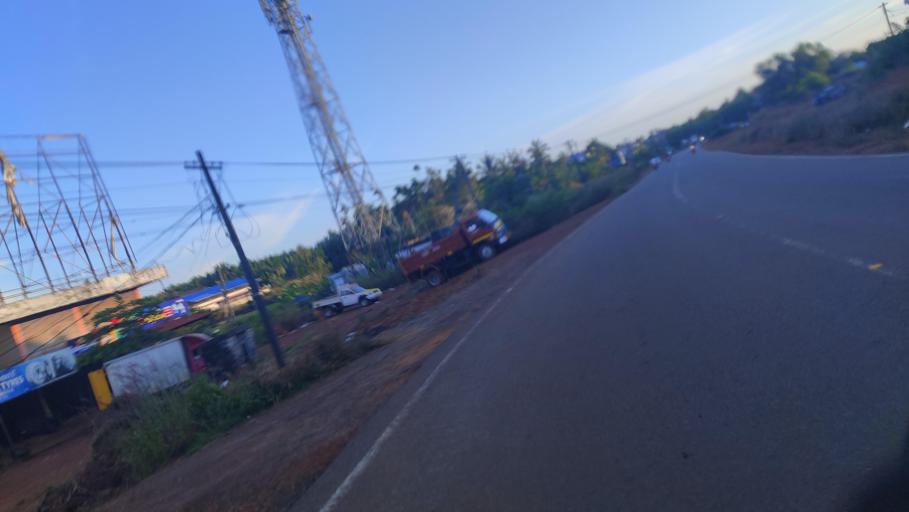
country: IN
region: Kerala
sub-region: Kasaragod District
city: Kannangad
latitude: 12.4067
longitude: 75.0966
